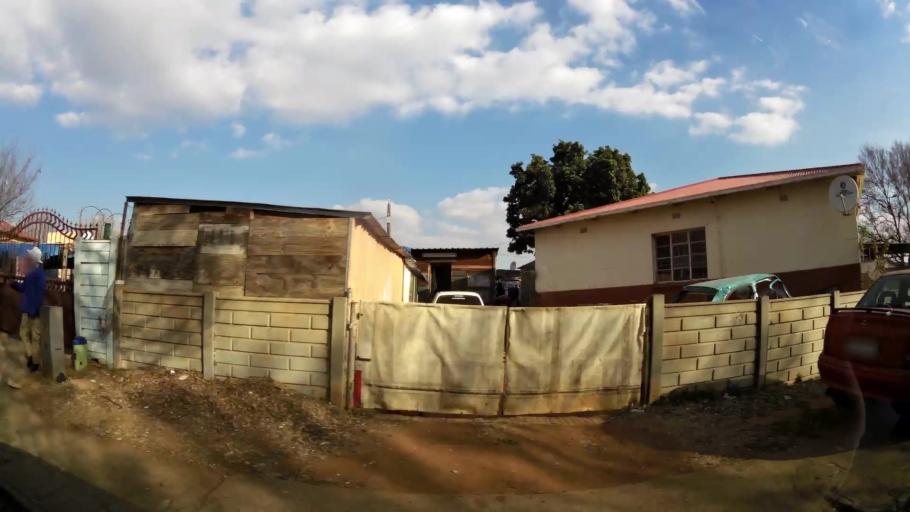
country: ZA
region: Gauteng
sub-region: West Rand District Municipality
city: Krugersdorp
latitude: -26.0953
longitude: 27.7562
